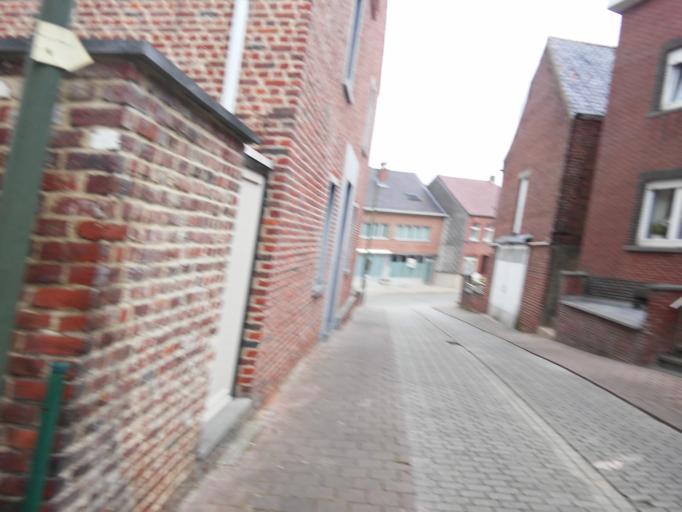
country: BE
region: Flanders
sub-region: Provincie Vlaams-Brabant
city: Herne
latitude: 50.7259
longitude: 4.0289
